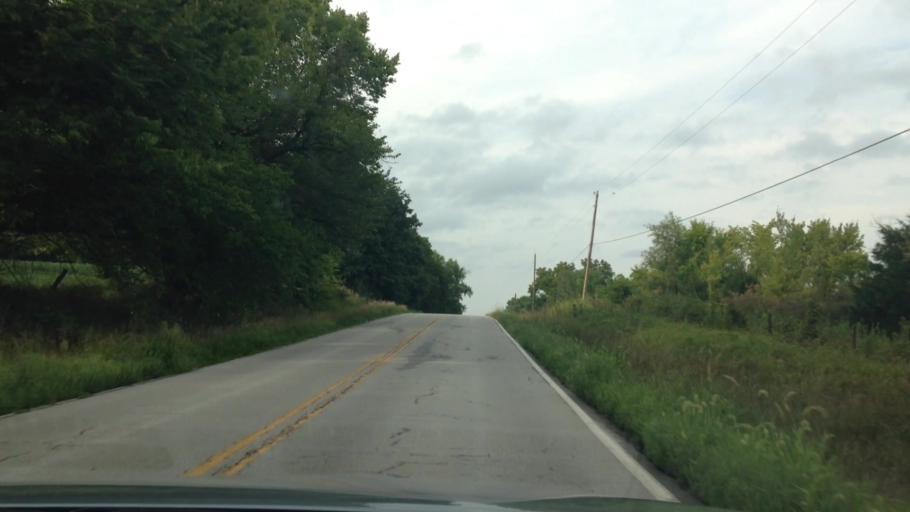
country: US
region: Missouri
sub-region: Clay County
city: Smithville
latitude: 39.3726
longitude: -94.6670
